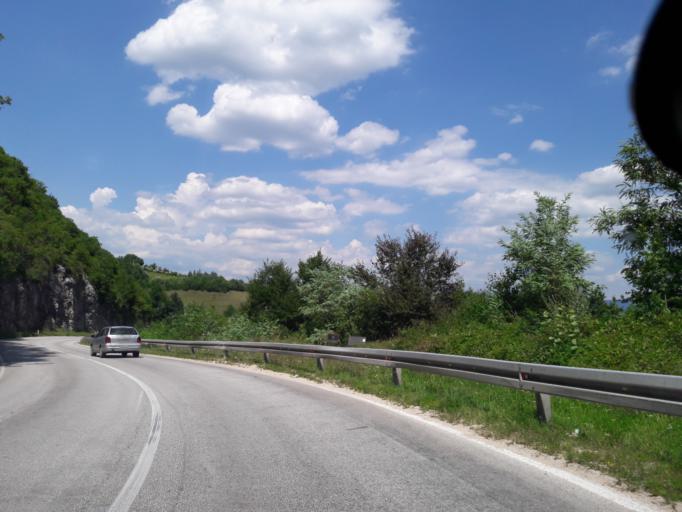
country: BA
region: Republika Srpska
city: Mrkonjic Grad
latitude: 44.4152
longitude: 17.0984
